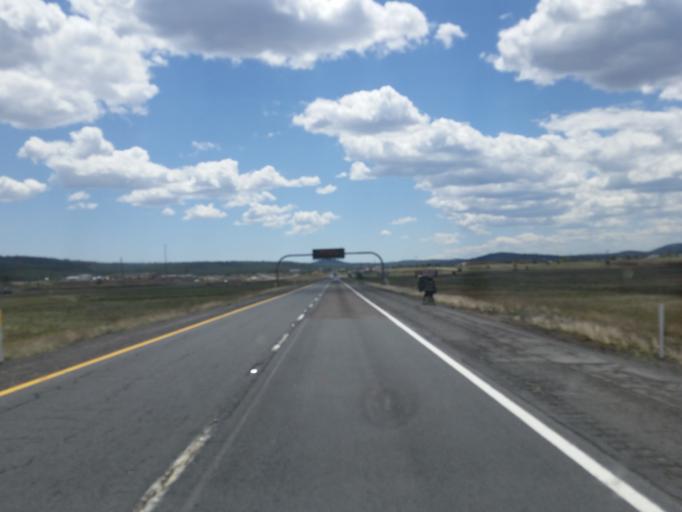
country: US
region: Arizona
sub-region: Coconino County
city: Parks
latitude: 35.2412
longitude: -111.8338
